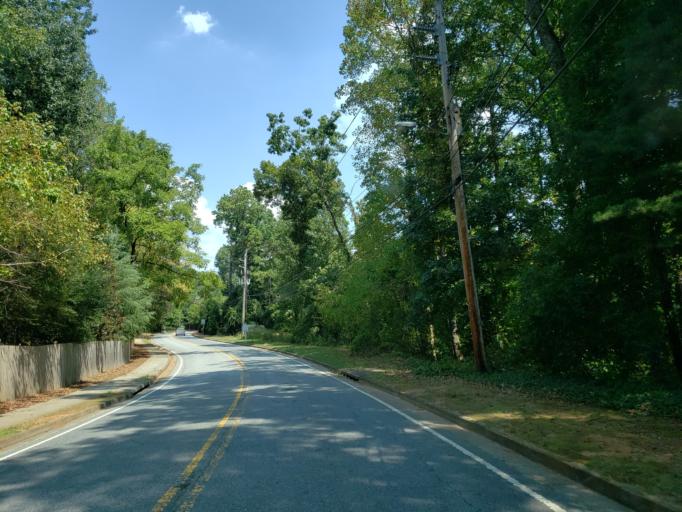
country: US
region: Georgia
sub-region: Cobb County
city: Vinings
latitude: 33.8990
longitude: -84.4246
